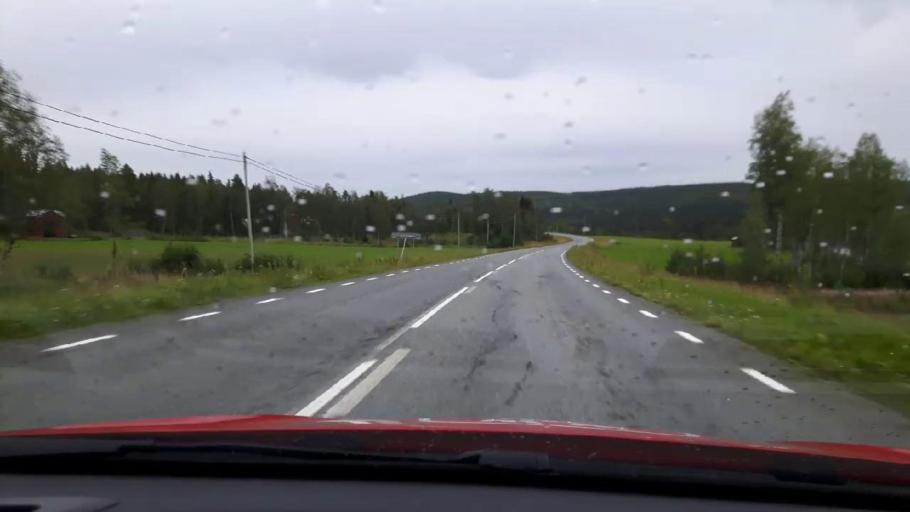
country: SE
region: Jaemtland
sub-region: Are Kommun
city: Jarpen
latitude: 63.4042
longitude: 13.3708
